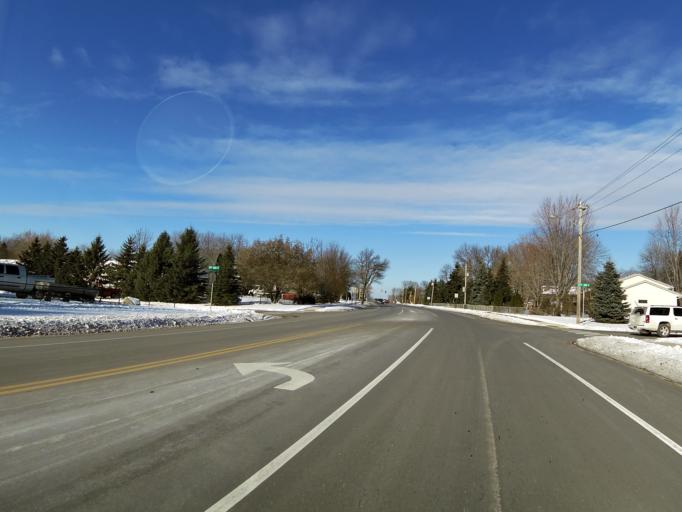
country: US
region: Minnesota
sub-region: Scott County
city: Shakopee
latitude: 44.7861
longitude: -93.5053
